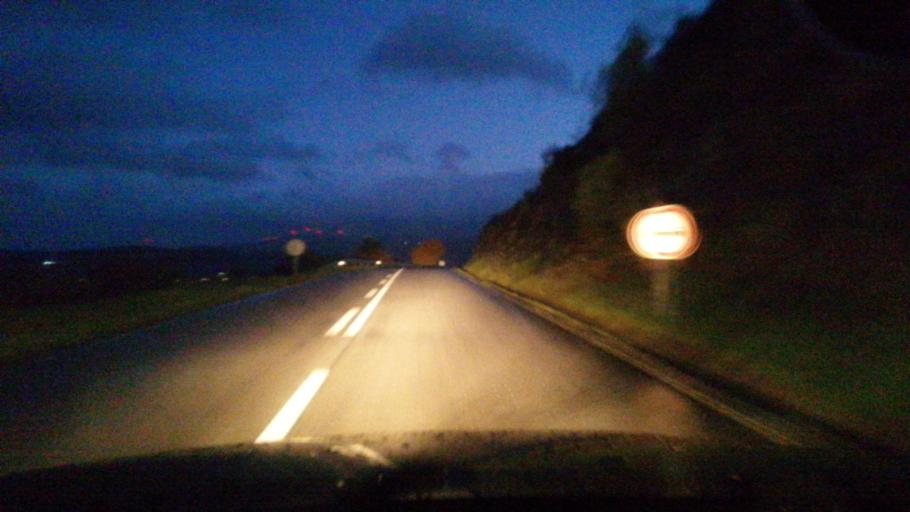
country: PT
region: Viseu
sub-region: Tabuaco
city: Tabuaco
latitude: 41.1301
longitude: -7.5196
